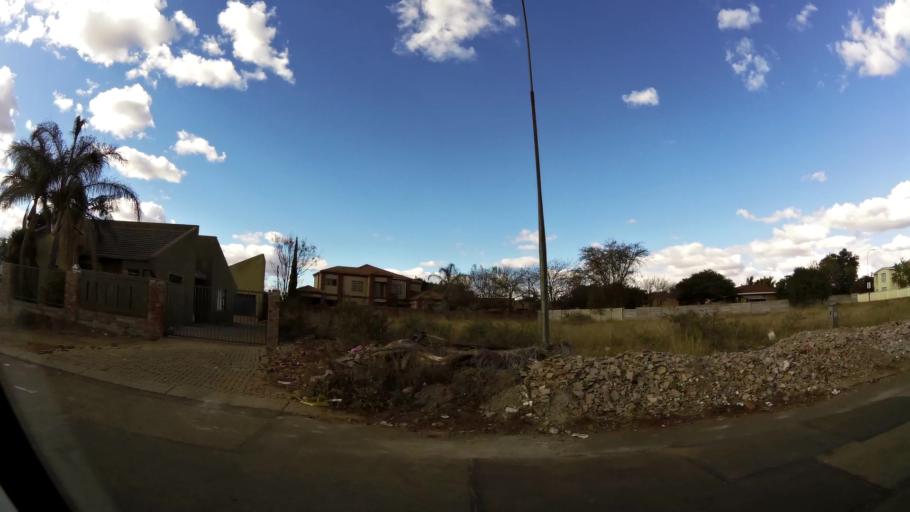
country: ZA
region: Limpopo
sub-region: Capricorn District Municipality
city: Polokwane
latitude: -23.9104
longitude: 29.4956
